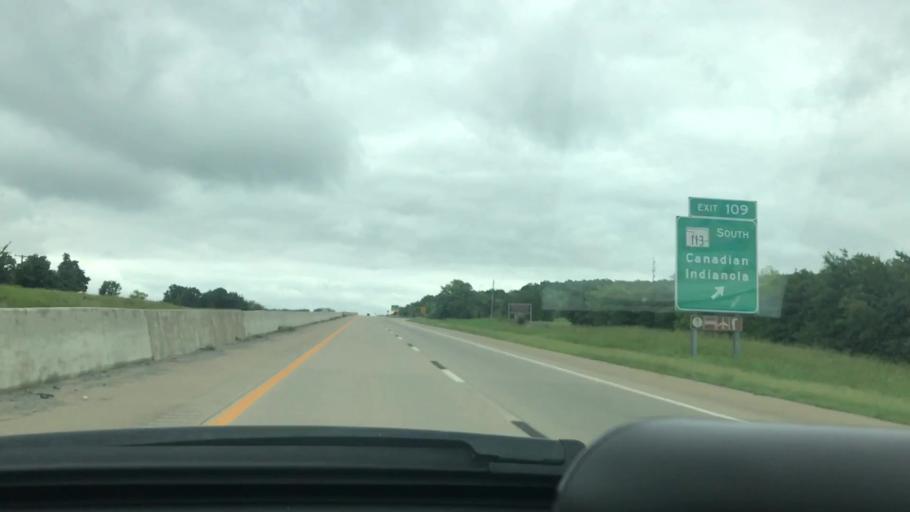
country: US
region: Oklahoma
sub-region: McIntosh County
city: Eufaula
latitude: 35.1674
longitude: -95.6517
